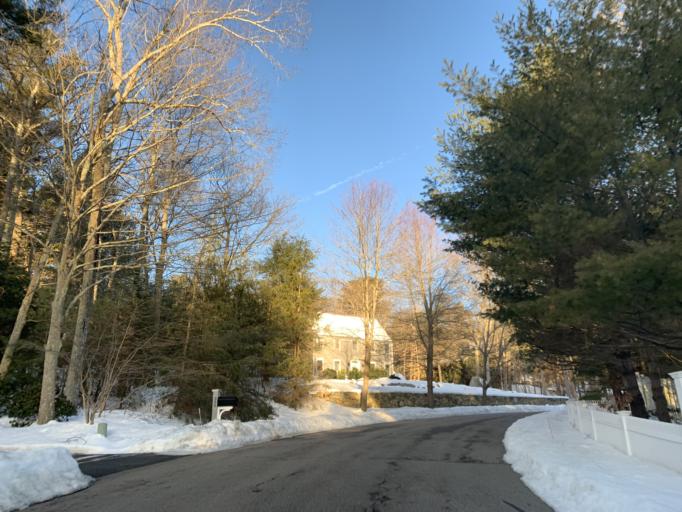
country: US
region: Massachusetts
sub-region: Norfolk County
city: Westwood
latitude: 42.2442
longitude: -71.2326
